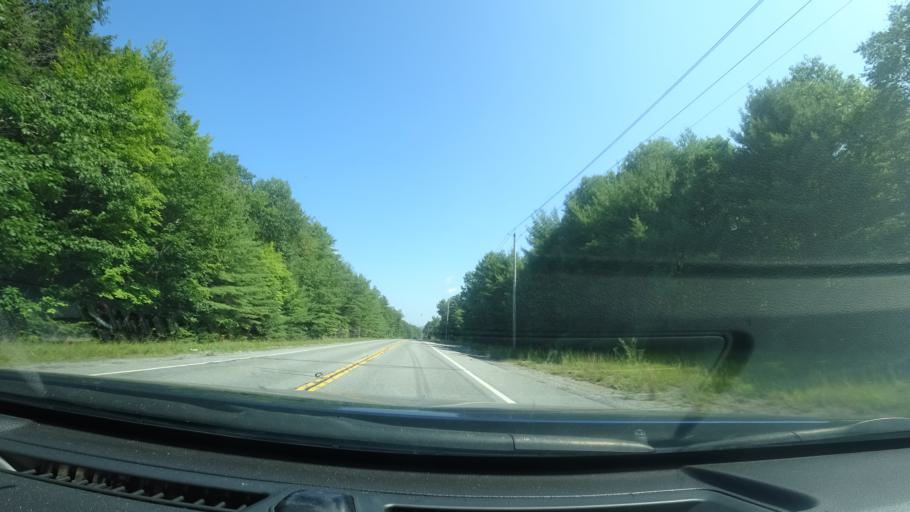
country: US
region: New York
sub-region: Warren County
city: Warrensburg
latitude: 43.6122
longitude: -73.8031
